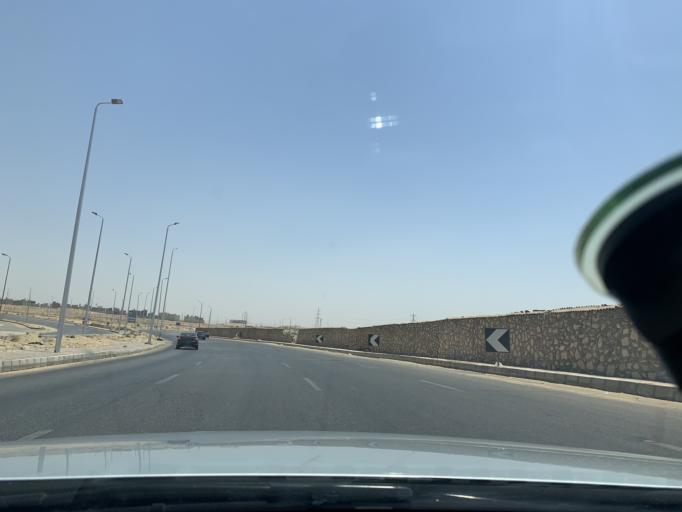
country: EG
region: Muhafazat al Qahirah
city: Halwan
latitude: 29.9777
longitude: 31.4691
